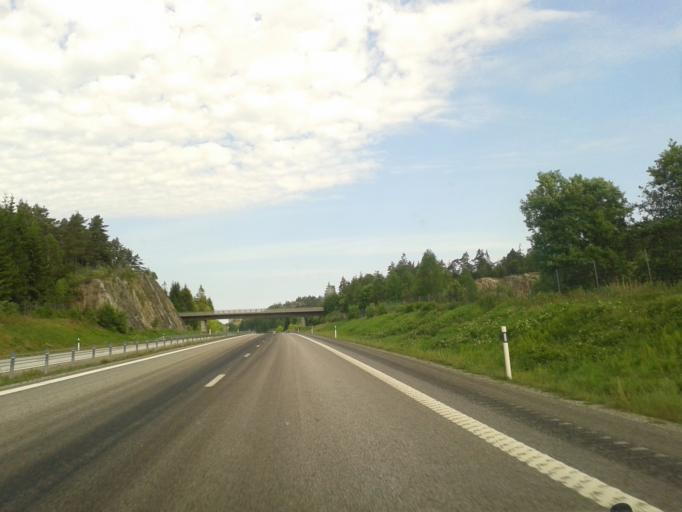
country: SE
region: Vaestra Goetaland
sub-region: Lysekils Kommun
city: Brastad
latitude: 58.5479
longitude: 11.5122
